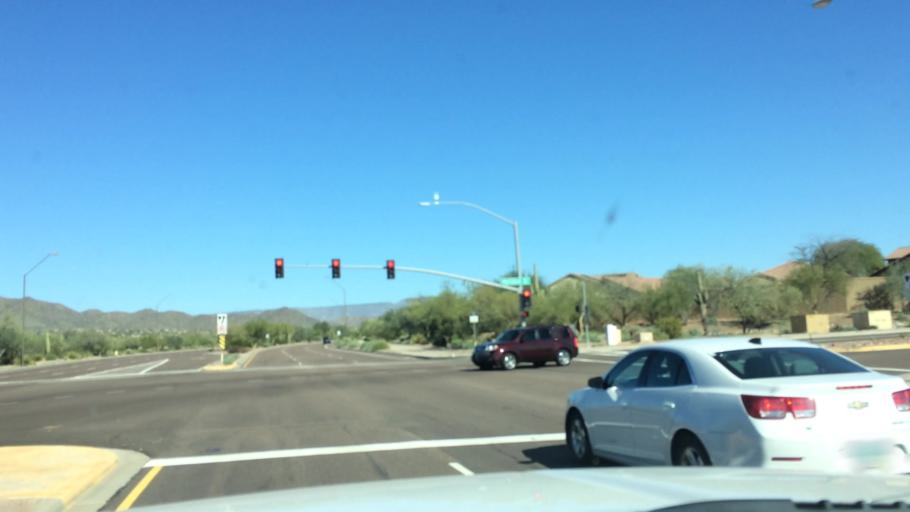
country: US
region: Arizona
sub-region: Maricopa County
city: Anthem
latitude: 33.8467
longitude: -112.1224
